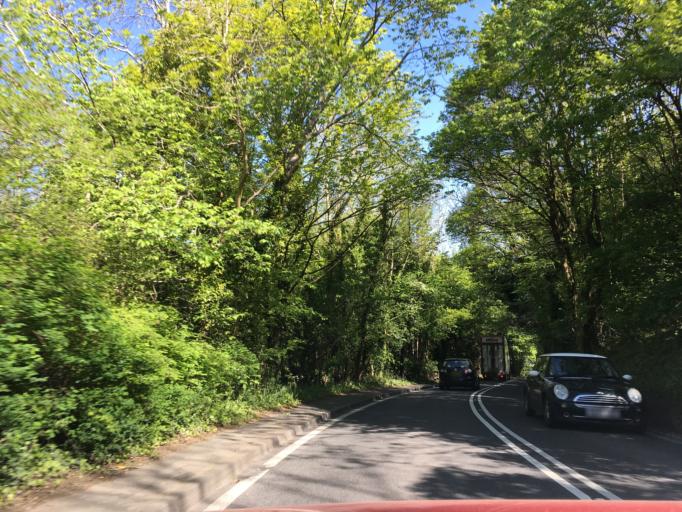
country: GB
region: England
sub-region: Gloucestershire
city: Nailsworth
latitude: 51.6880
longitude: -2.2220
